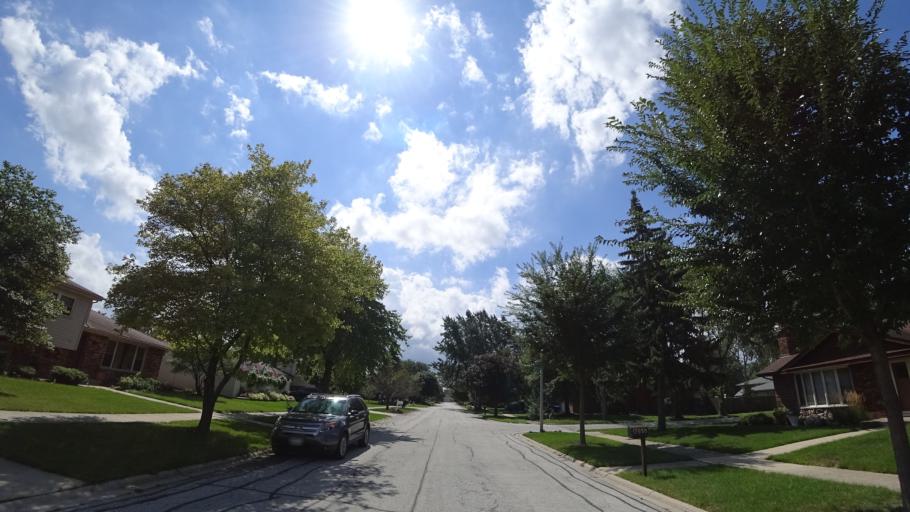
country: US
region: Illinois
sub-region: Cook County
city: Tinley Park
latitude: 41.5648
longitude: -87.7763
